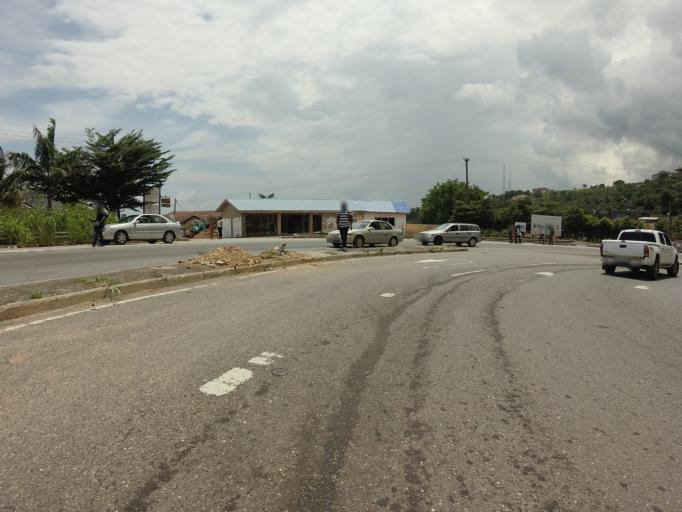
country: GH
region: Eastern
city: Aburi
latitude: 5.8013
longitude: -0.1824
